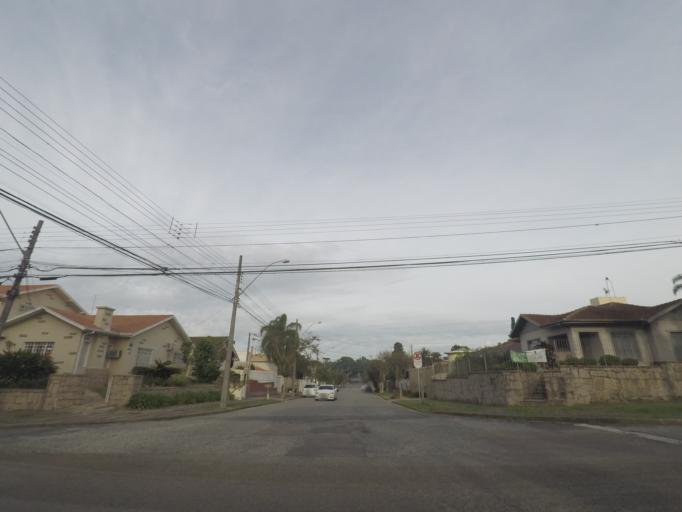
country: BR
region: Parana
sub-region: Curitiba
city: Curitiba
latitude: -25.4404
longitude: -49.2921
